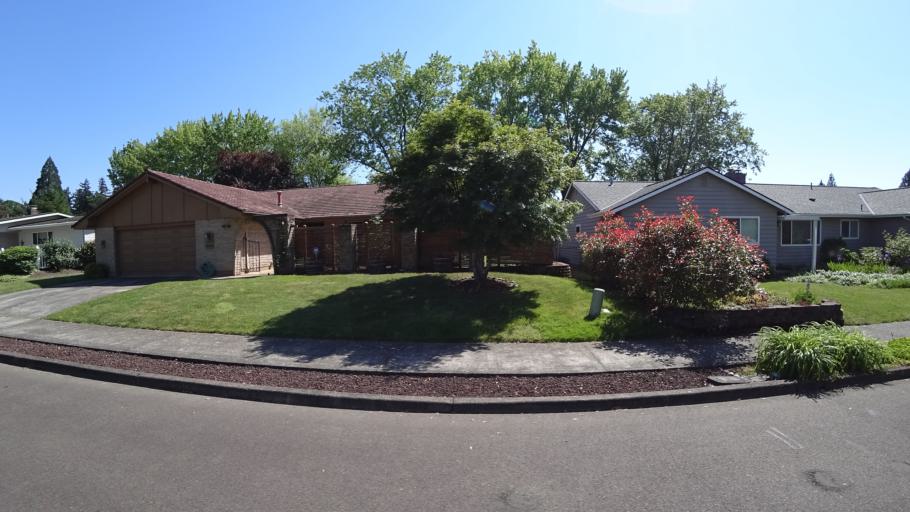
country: US
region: Oregon
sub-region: Washington County
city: Rockcreek
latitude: 45.5531
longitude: -122.8729
